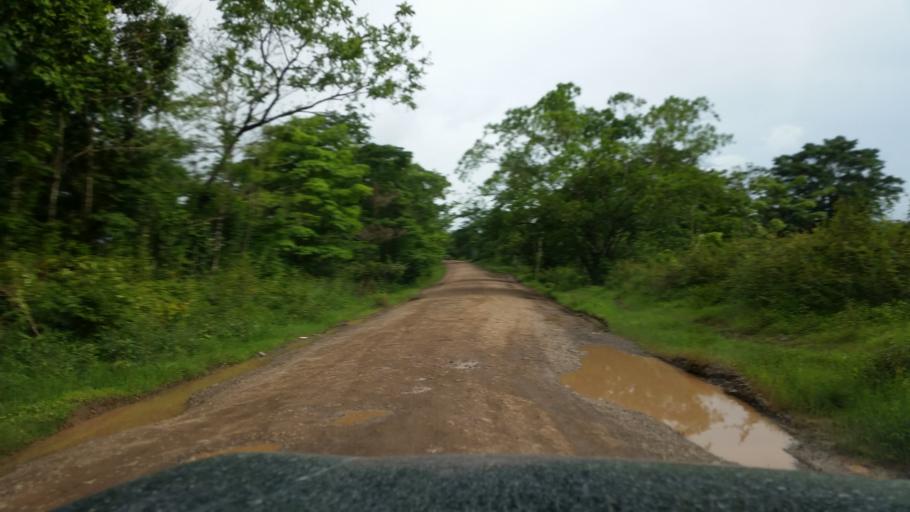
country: NI
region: Atlantico Norte (RAAN)
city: Siuna
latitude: 13.4251
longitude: -84.8529
